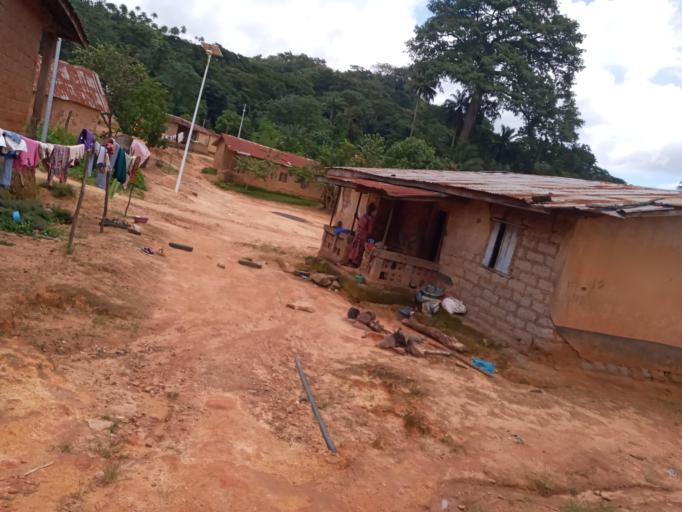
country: SL
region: Eastern Province
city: Tombu
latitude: 8.6253
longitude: -10.8235
